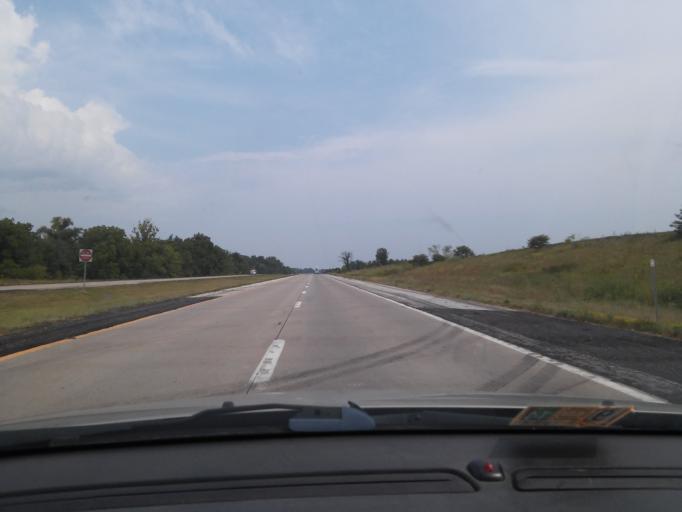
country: US
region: Missouri
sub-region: Callaway County
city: Fulton
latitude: 38.9890
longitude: -91.8937
